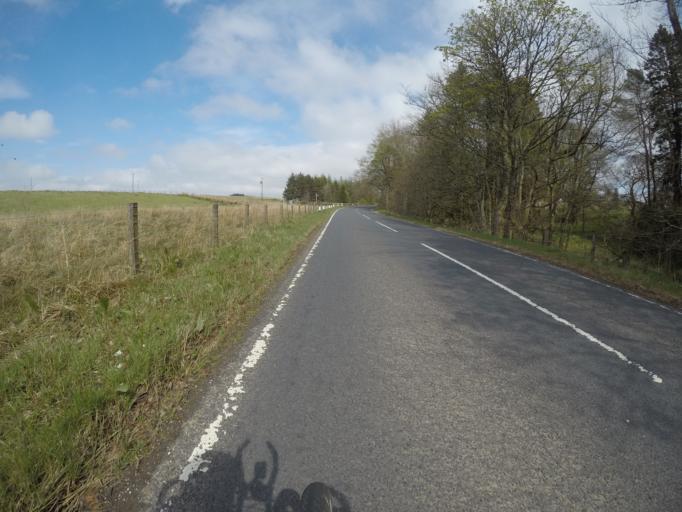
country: GB
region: Scotland
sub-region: East Renfrewshire
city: Neilston
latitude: 55.7190
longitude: -4.4340
